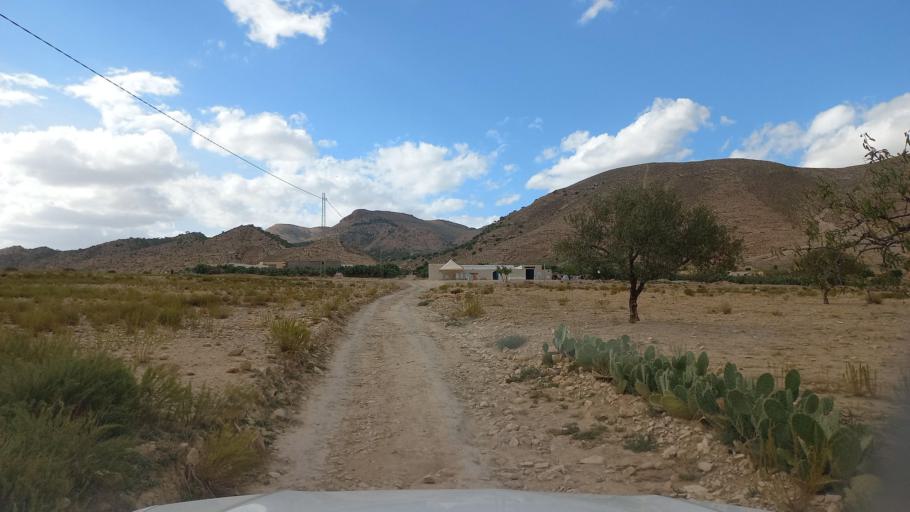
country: TN
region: Al Qasrayn
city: Sbiba
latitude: 35.4506
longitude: 9.0661
